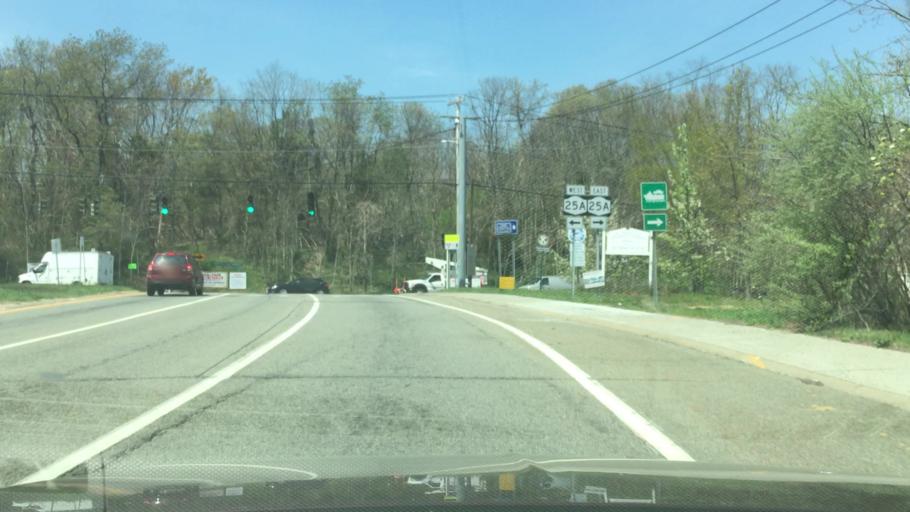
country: US
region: New York
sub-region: Suffolk County
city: Setauket-East Setauket
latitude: 40.9258
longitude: -73.1196
